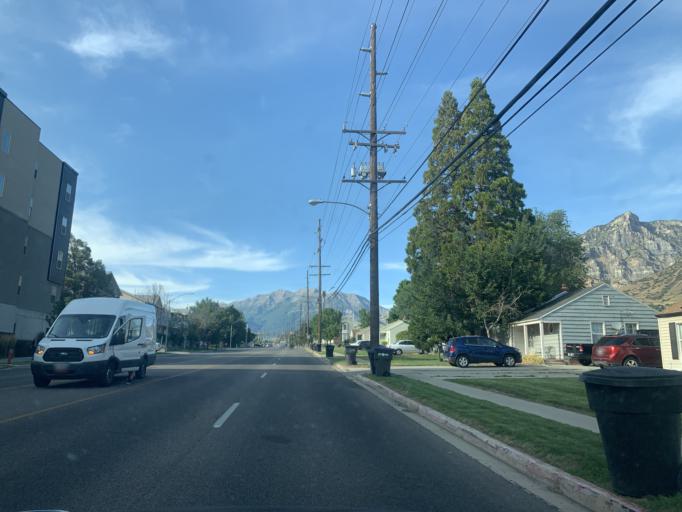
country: US
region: Utah
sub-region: Utah County
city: Provo
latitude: 40.2436
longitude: -111.6431
